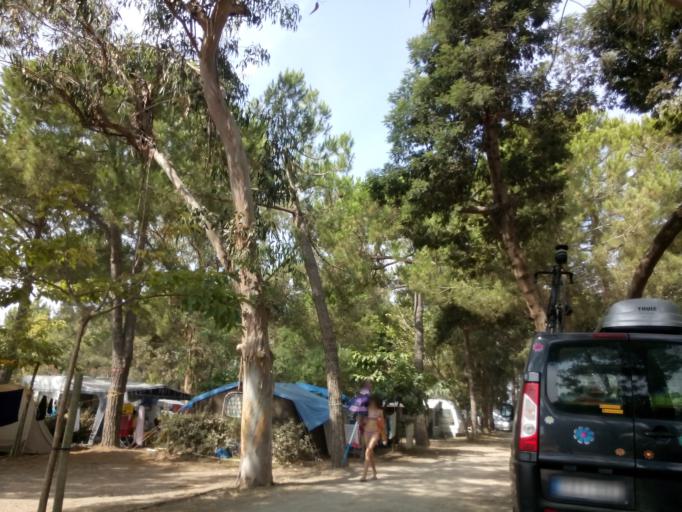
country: FR
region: Corsica
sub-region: Departement de la Haute-Corse
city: Aleria
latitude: 42.1094
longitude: 9.5502
